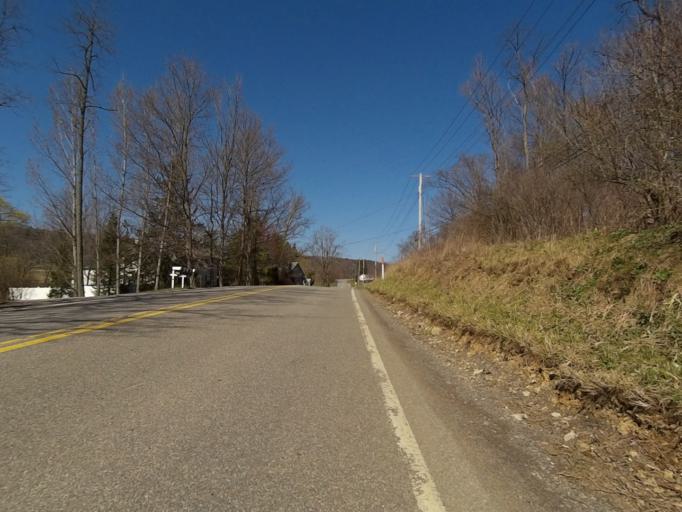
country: US
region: Pennsylvania
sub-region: Centre County
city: Stormstown
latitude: 40.8042
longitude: -77.9986
